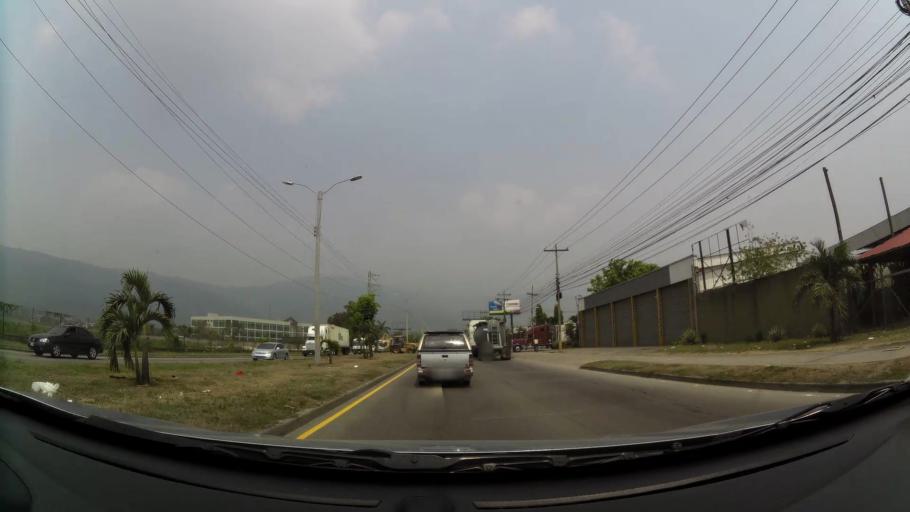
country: HN
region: Cortes
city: San Pedro Sula
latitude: 15.4737
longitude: -88.0160
